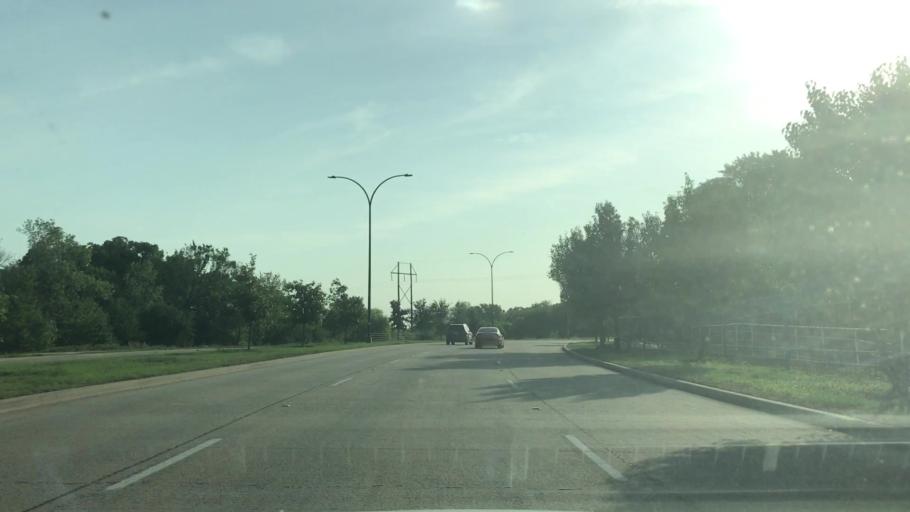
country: US
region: Texas
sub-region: Tarrant County
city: Arlington
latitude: 32.7706
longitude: -97.1461
